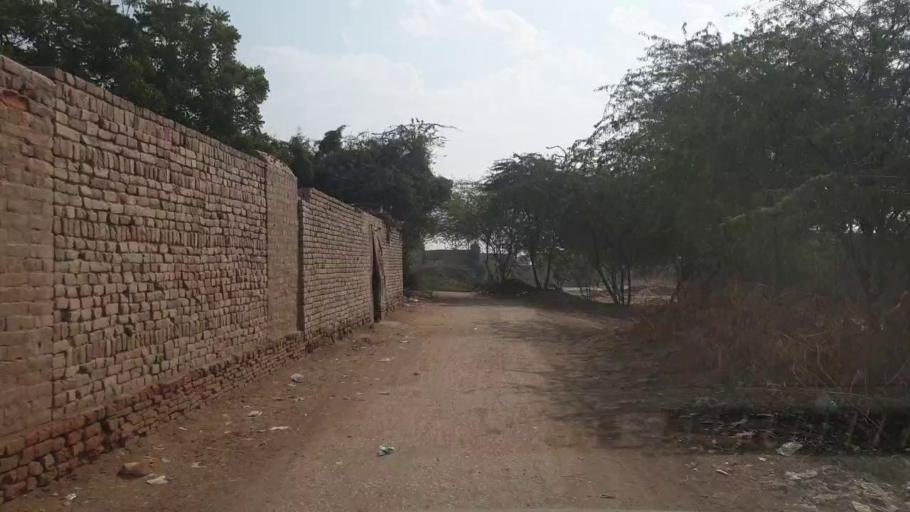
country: PK
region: Sindh
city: Hala
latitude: 25.7934
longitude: 68.4219
